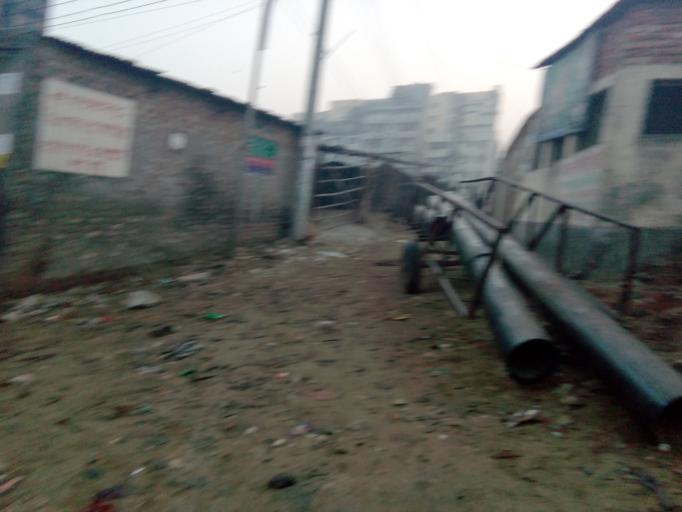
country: BD
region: Dhaka
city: Paltan
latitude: 23.7467
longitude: 90.4195
